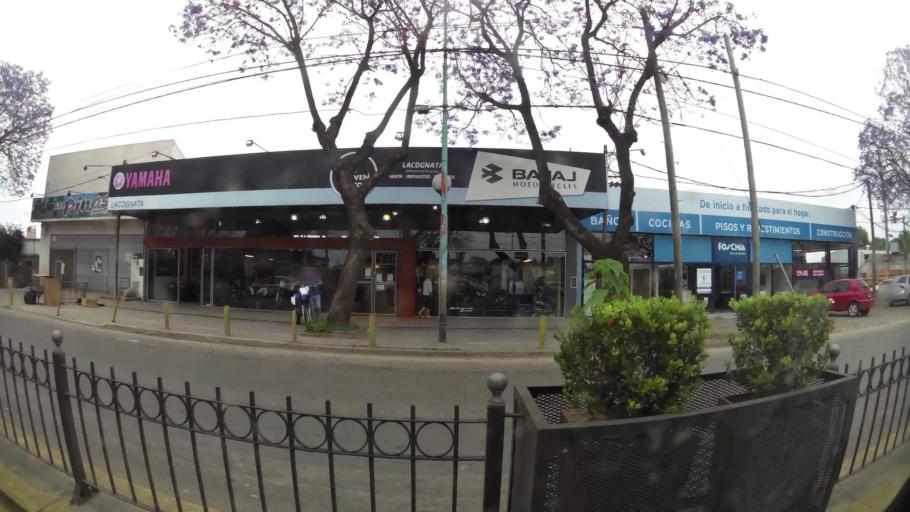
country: AR
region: Buenos Aires
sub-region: Partido de Zarate
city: Zarate
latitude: -34.1069
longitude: -59.0218
